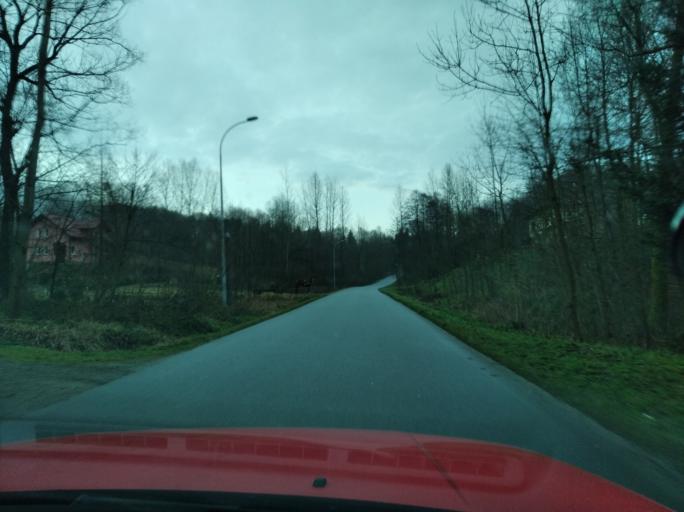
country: PL
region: Subcarpathian Voivodeship
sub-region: Powiat strzyzowski
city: Gwoznica Gorna
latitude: 49.8159
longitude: 22.0061
